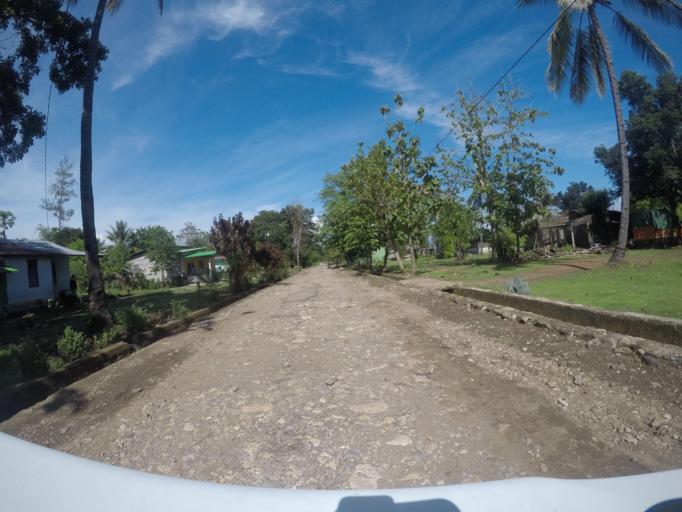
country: TL
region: Bobonaro
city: Maliana
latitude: -8.9877
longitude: 125.2001
